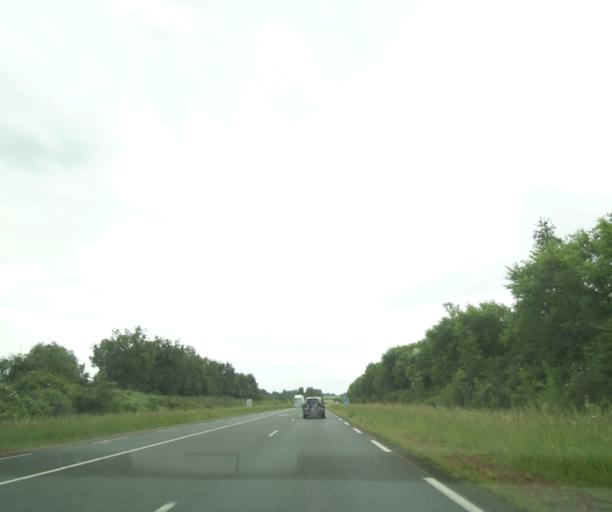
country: FR
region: Poitou-Charentes
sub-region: Departement des Deux-Sevres
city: Airvault
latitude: 46.8064
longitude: -0.2117
